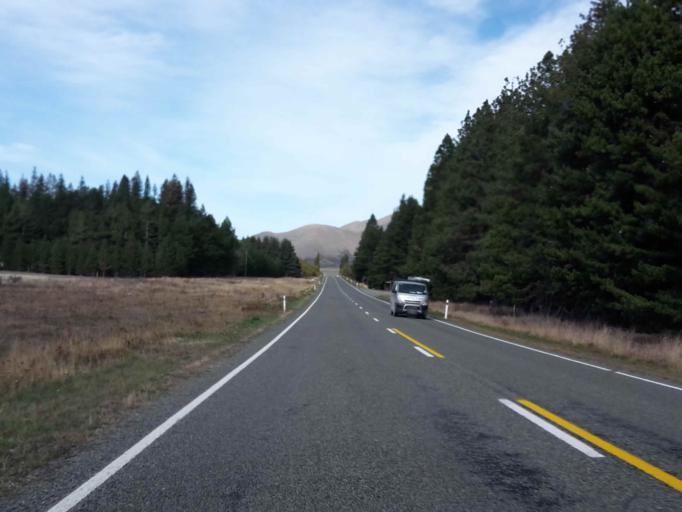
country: NZ
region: Canterbury
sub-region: Timaru District
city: Pleasant Point
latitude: -44.0849
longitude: 170.5405
